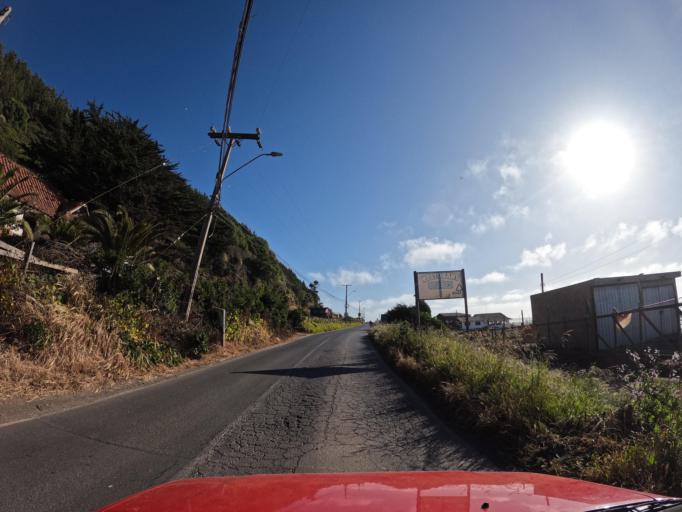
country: CL
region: Maule
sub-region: Provincia de Talca
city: Constitucion
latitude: -34.8911
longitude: -72.1746
